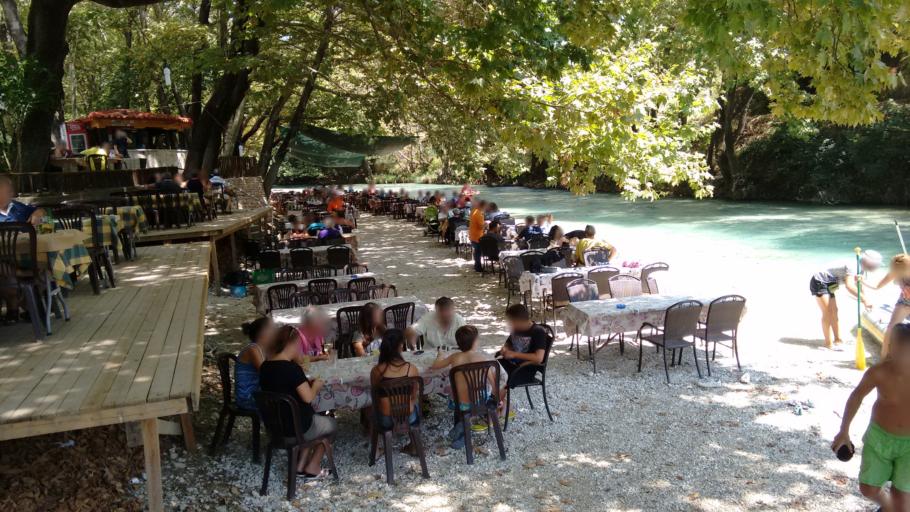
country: GR
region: Epirus
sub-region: Nomos Prevezis
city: Kanalaki
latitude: 39.3225
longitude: 20.6080
